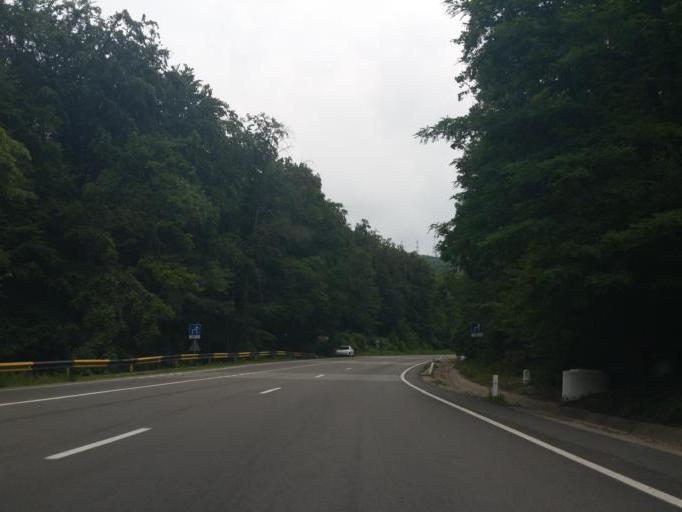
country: RO
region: Salaj
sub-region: Comuna Treznea
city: Treznea
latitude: 47.1424
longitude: 23.1013
